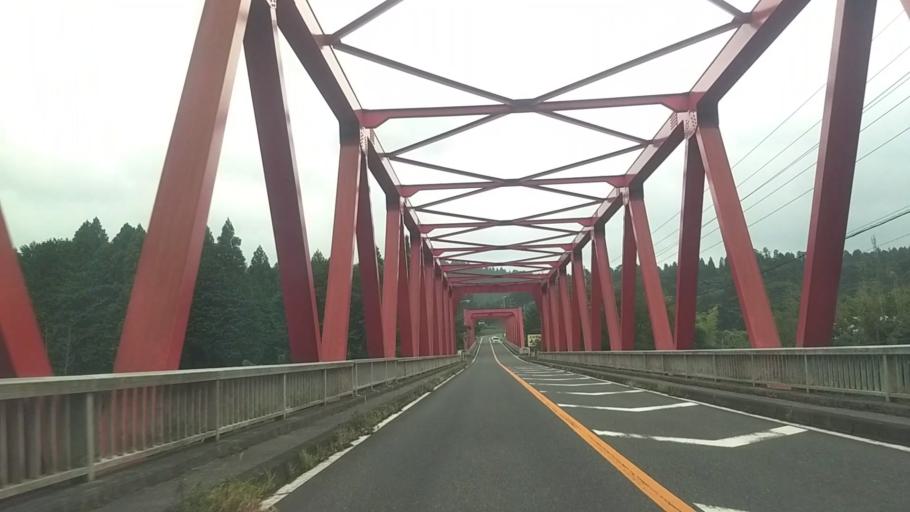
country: JP
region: Chiba
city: Kawaguchi
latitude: 35.2220
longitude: 140.0723
